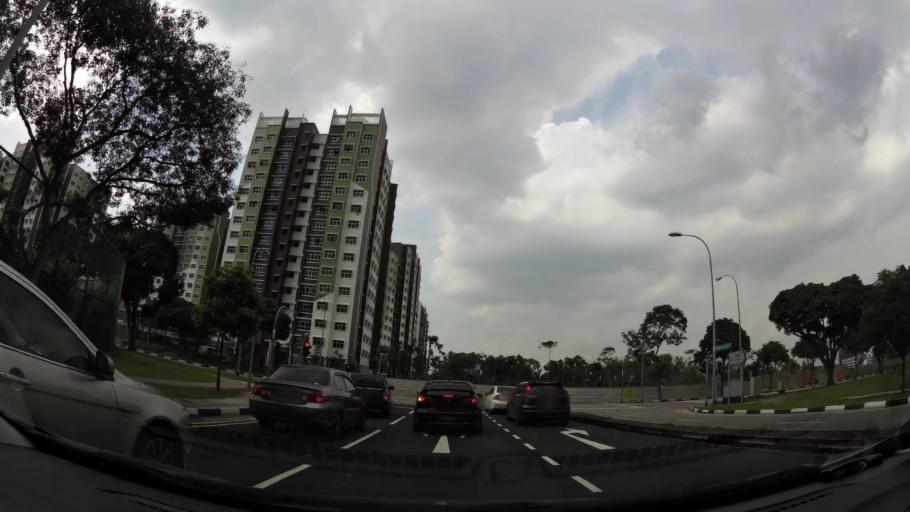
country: SG
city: Singapore
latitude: 1.3516
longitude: 103.9304
